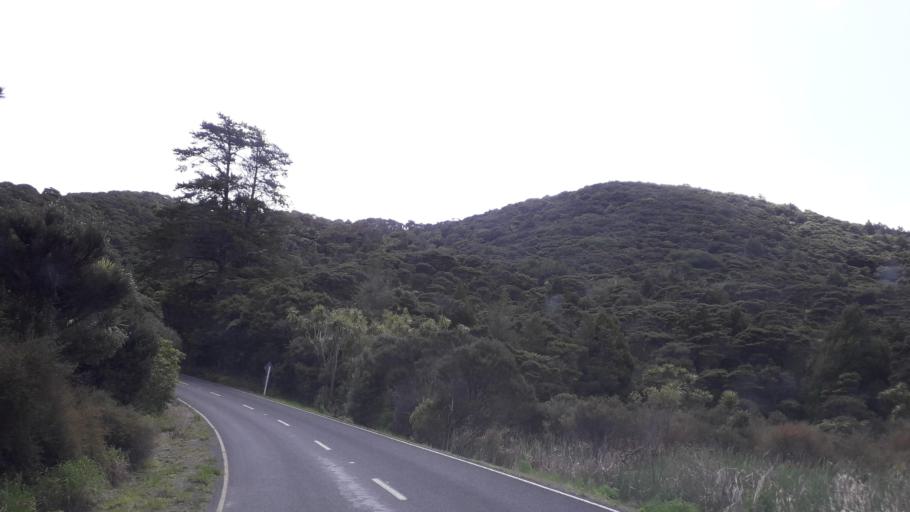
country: NZ
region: Northland
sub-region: Far North District
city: Paihia
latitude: -35.2556
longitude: 174.2674
